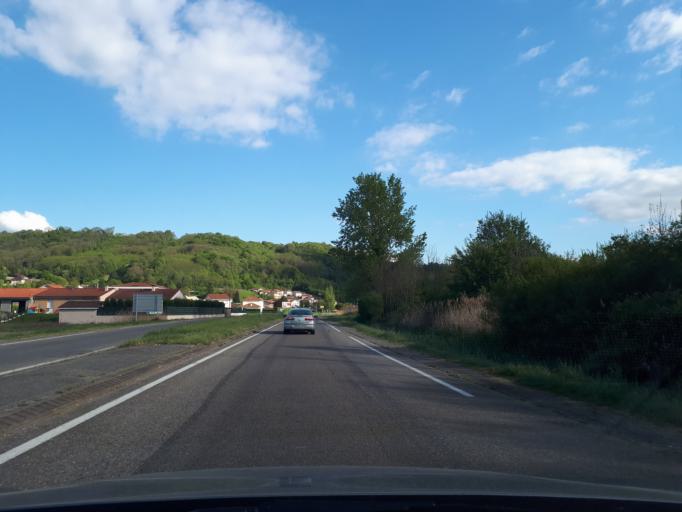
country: FR
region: Rhone-Alpes
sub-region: Departement de l'Isere
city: Bourgoin-Jallieu
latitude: 45.6159
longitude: 5.2700
